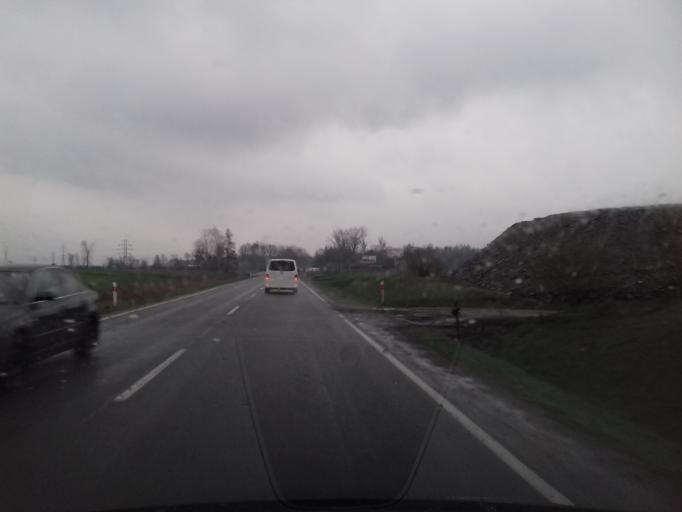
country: PL
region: Lesser Poland Voivodeship
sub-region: Powiat nowosadecki
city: Stary Sacz
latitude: 49.5552
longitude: 20.6548
